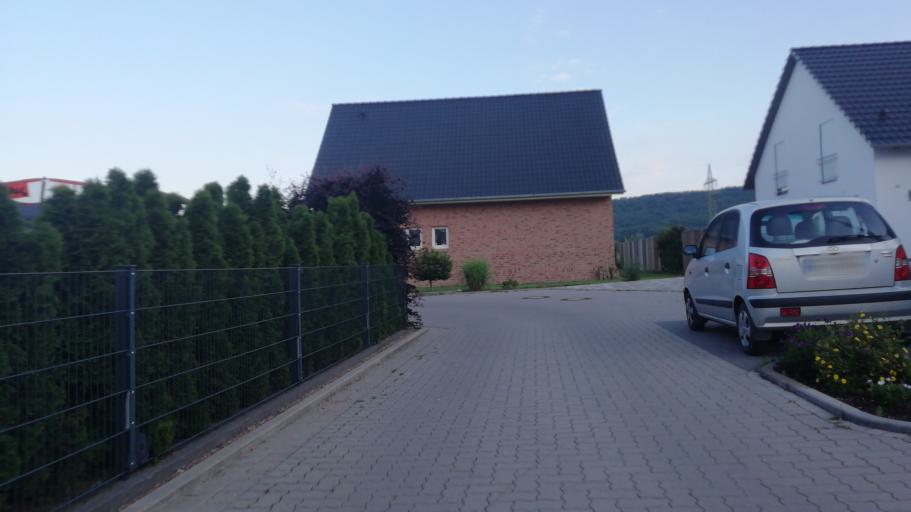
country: DE
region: North Rhine-Westphalia
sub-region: Regierungsbezirk Detmold
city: Minden
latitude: 52.2681
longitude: 8.8981
